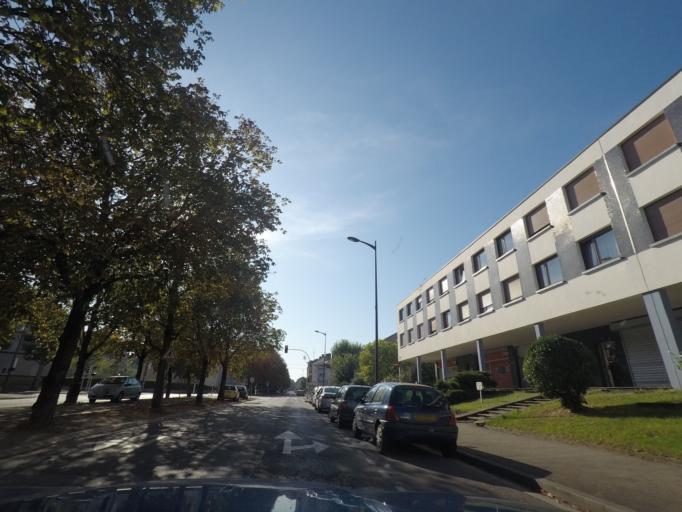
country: FR
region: Lorraine
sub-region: Departement de la Moselle
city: Thionville
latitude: 49.3615
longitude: 6.1570
